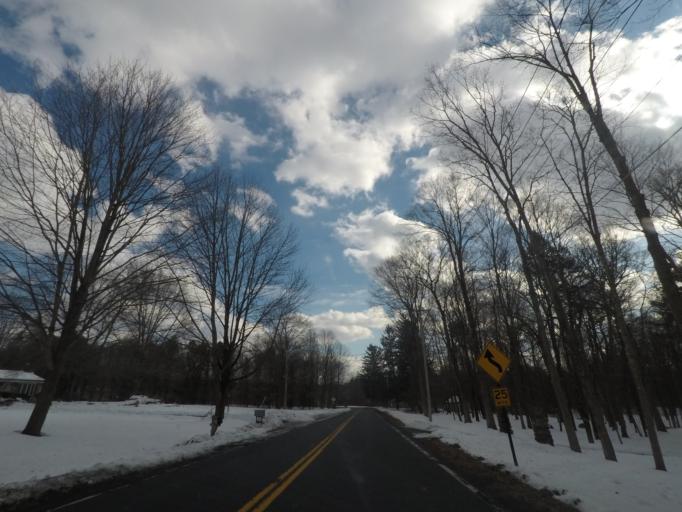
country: US
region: New York
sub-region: Schenectady County
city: Niskayuna
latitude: 42.8213
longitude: -73.8540
